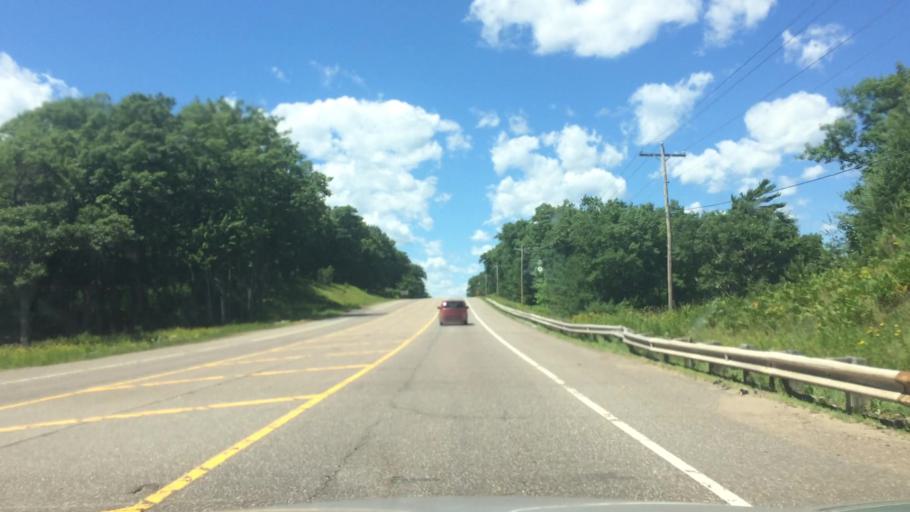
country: US
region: Wisconsin
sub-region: Vilas County
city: Lac du Flambeau
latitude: 45.7916
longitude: -89.7125
